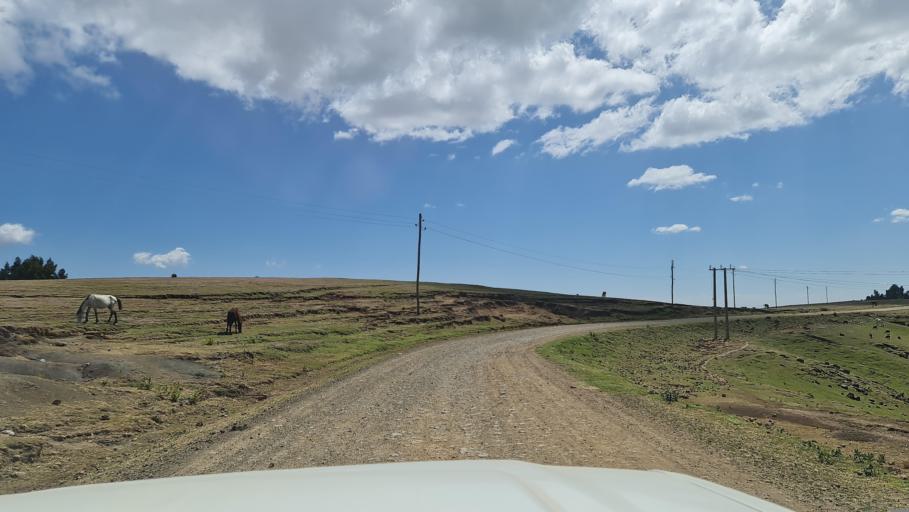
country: ET
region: Amhara
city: Debark'
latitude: 13.1970
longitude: 37.9749
